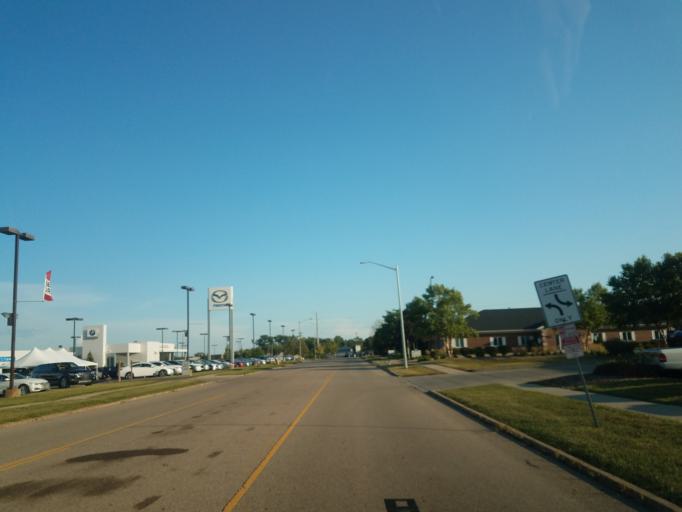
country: US
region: Illinois
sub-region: McLean County
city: Bloomington
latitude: 40.4584
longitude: -88.9754
